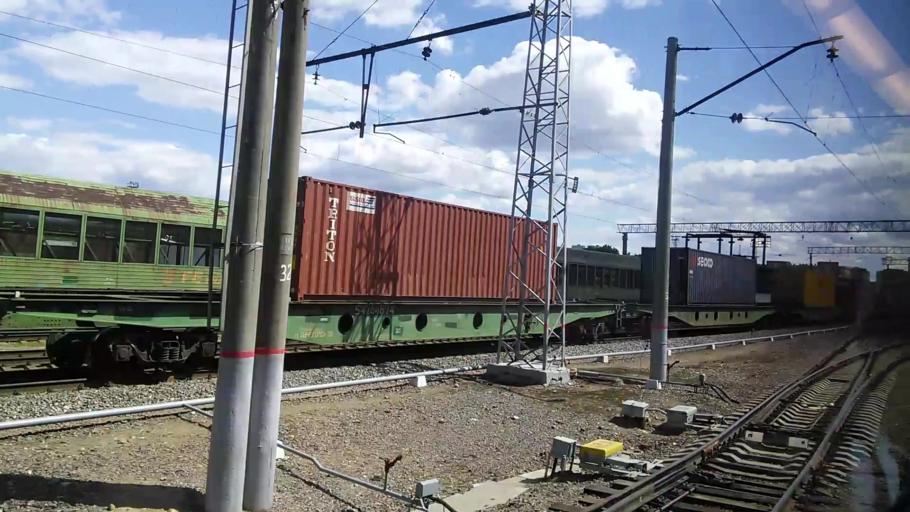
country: RU
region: Moscow
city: Mar'ina Roshcha
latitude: 55.8000
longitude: 37.5886
